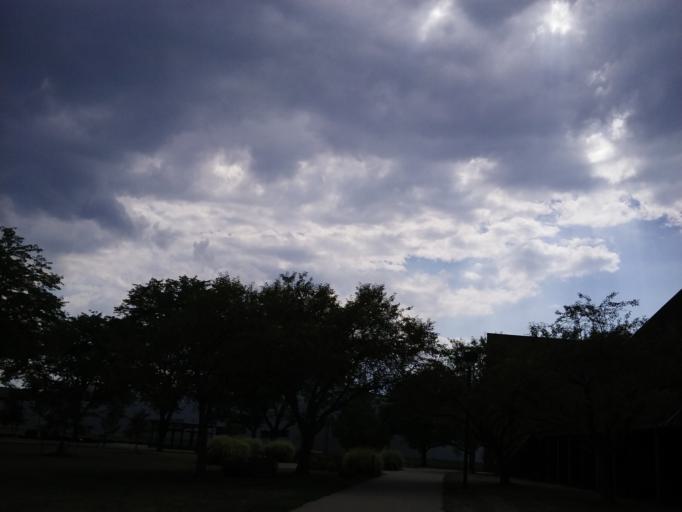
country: US
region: Ohio
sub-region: Wood County
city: Bowling Green
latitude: 41.3787
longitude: -83.6324
